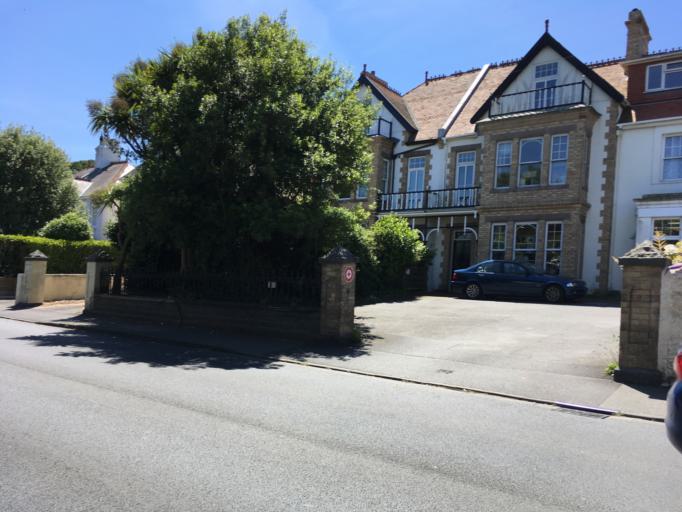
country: GG
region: St Peter Port
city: Saint Peter Port
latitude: 49.4591
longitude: -2.5543
